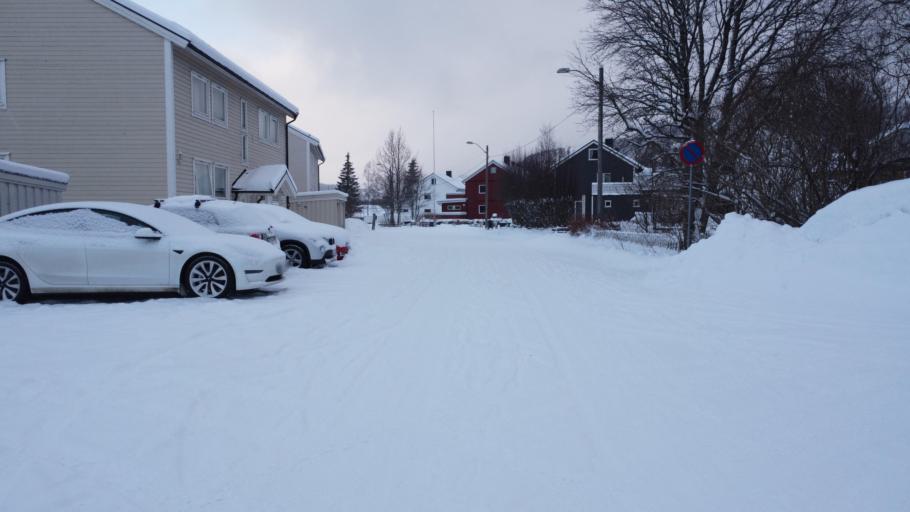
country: NO
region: Nordland
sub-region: Rana
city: Mo i Rana
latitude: 66.3196
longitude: 14.1630
